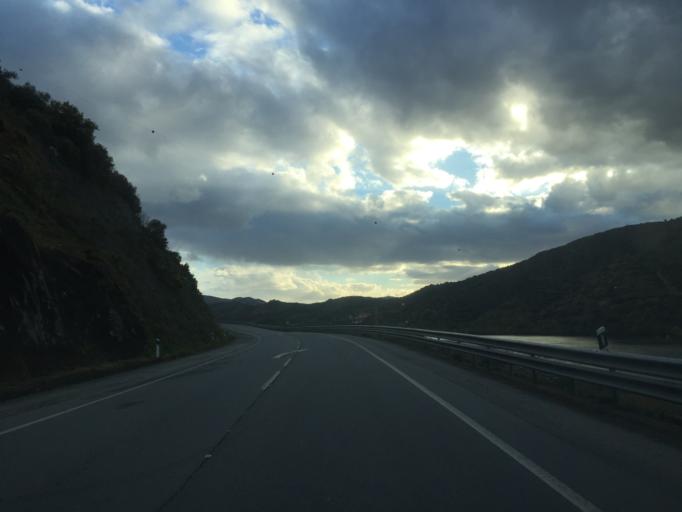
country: PT
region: Braganca
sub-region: Torre de Moncorvo
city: Torre de Moncorvo
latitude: 41.1461
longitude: -7.1176
